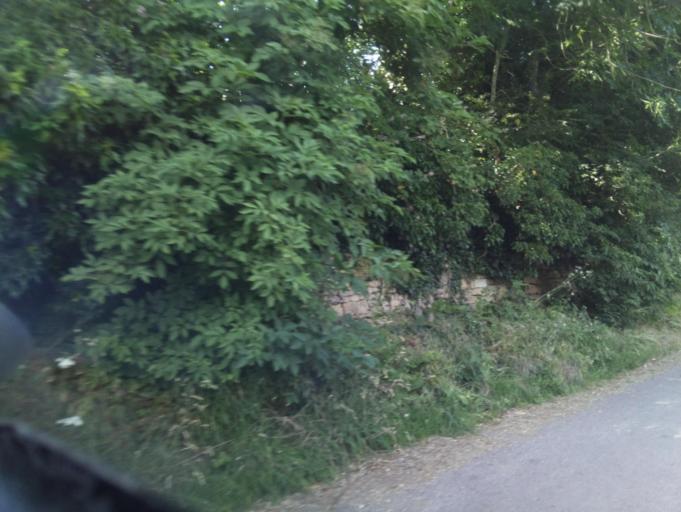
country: GB
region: England
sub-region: Gloucestershire
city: Chipping Campden
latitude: 52.0108
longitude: -1.7653
